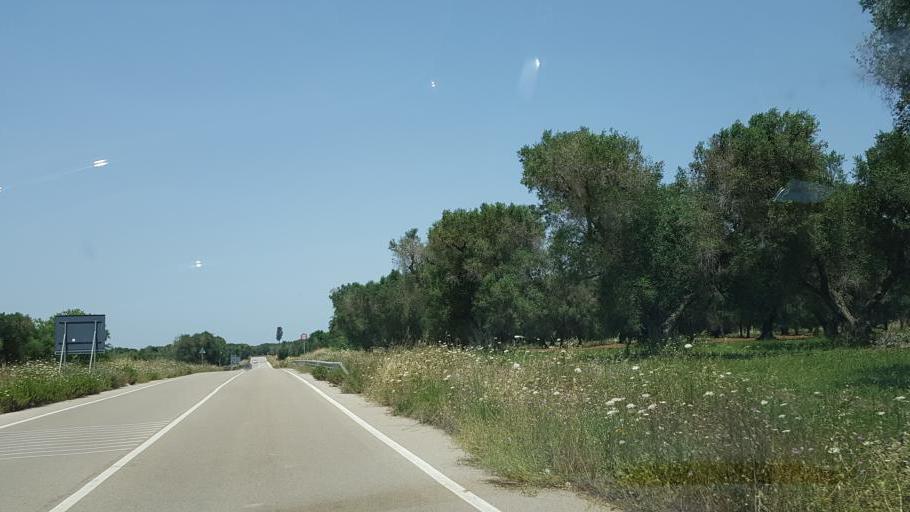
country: IT
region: Apulia
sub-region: Provincia di Brindisi
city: San Pancrazio Salentino
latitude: 40.4873
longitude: 17.8337
